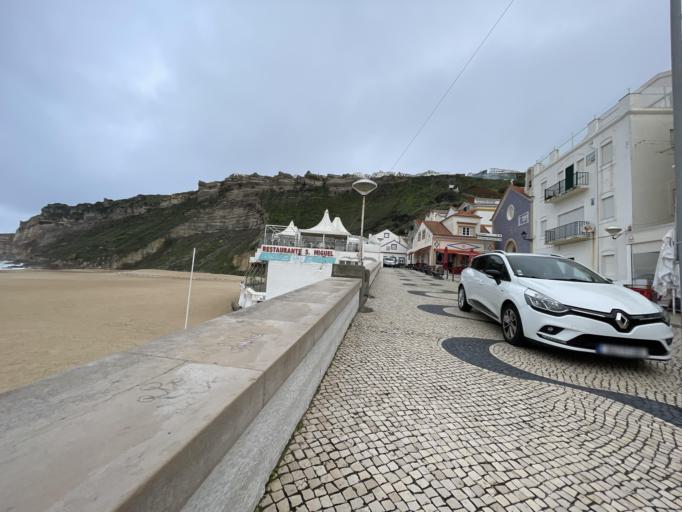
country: PT
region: Leiria
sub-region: Nazare
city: Nazare
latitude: 39.6024
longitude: -9.0742
